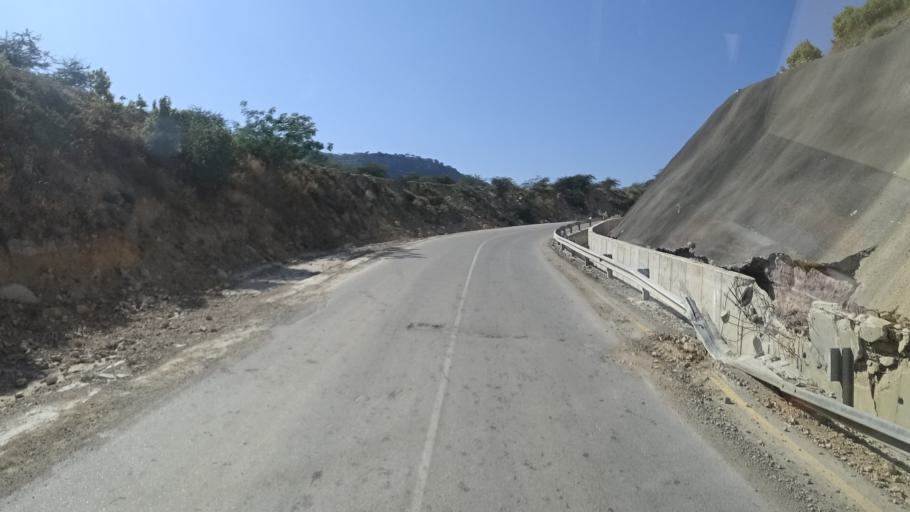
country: OM
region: Zufar
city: Salalah
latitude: 17.0551
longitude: 54.6115
